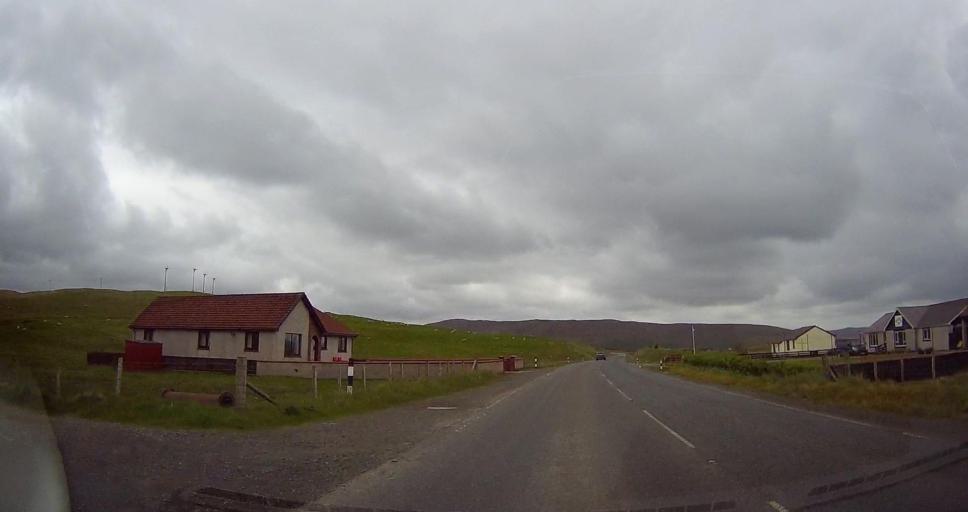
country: GB
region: Scotland
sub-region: Shetland Islands
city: Lerwick
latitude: 60.3787
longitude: -1.3409
